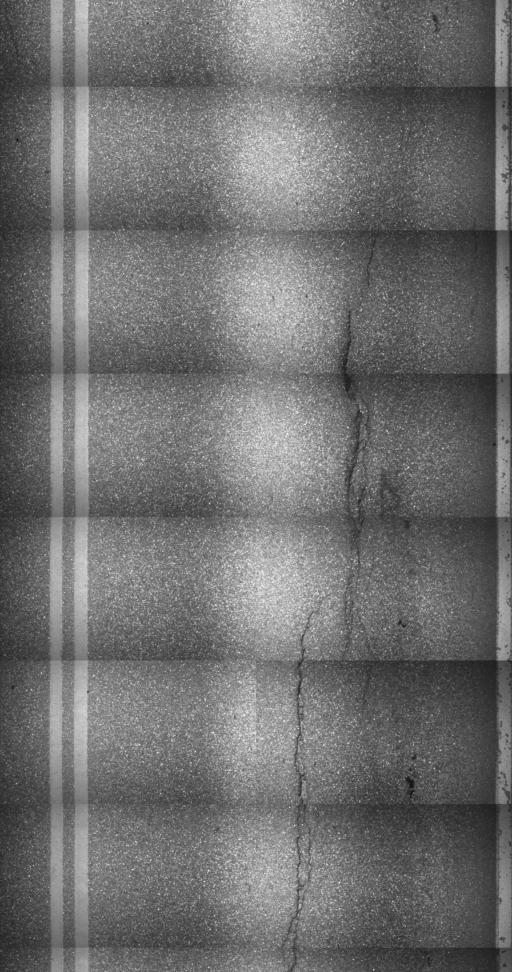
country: US
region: Vermont
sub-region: Chittenden County
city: Jericho
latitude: 44.5845
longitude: -72.9399
